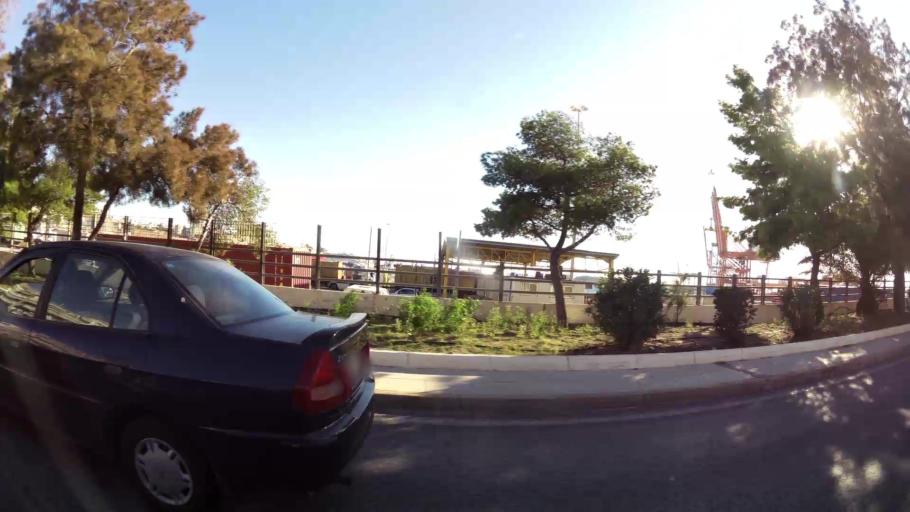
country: GR
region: Attica
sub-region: Nomos Piraios
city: Keratsini
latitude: 37.9625
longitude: 23.6048
